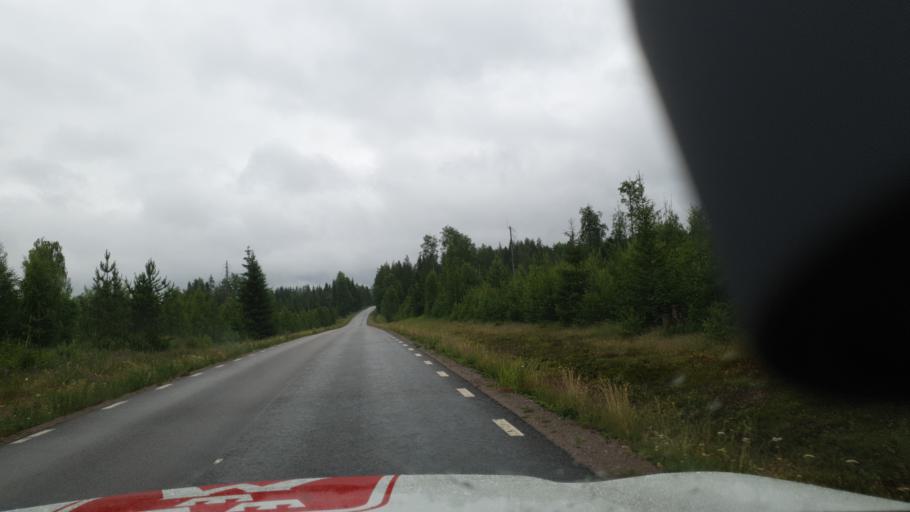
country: SE
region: Vaesterbotten
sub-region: Vannas Kommun
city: Vannasby
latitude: 63.8026
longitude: 19.8500
